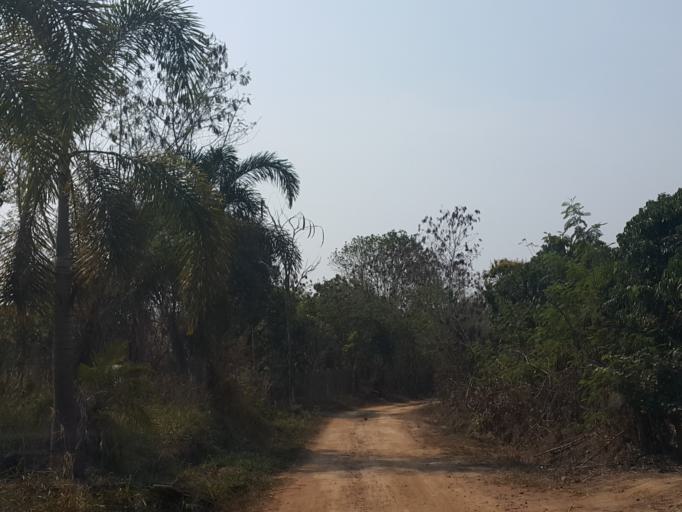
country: TH
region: Chiang Mai
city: Hang Dong
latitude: 18.7292
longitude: 98.8536
